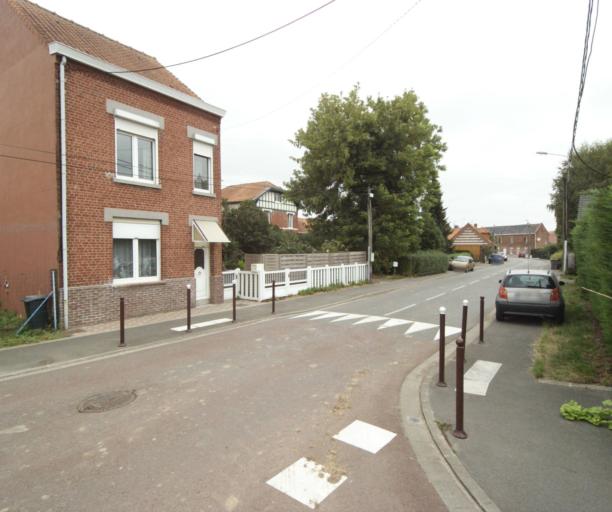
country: FR
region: Nord-Pas-de-Calais
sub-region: Departement du Nord
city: Chereng
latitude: 50.6164
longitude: 3.2110
